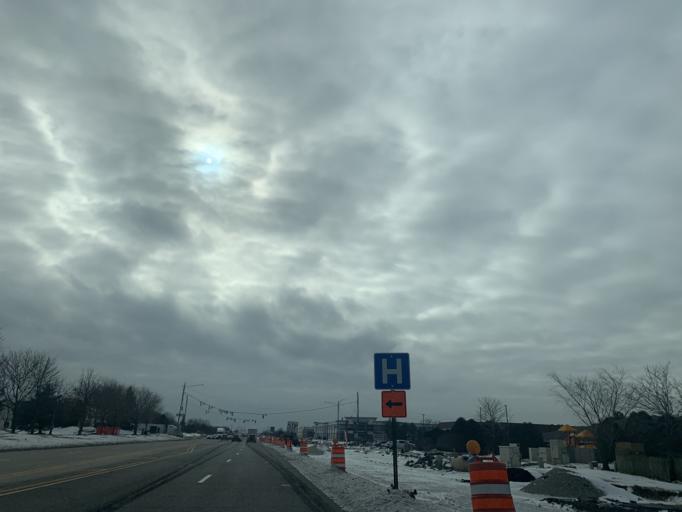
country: US
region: Illinois
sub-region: Will County
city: Romeoville
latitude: 41.6697
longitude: -88.1253
